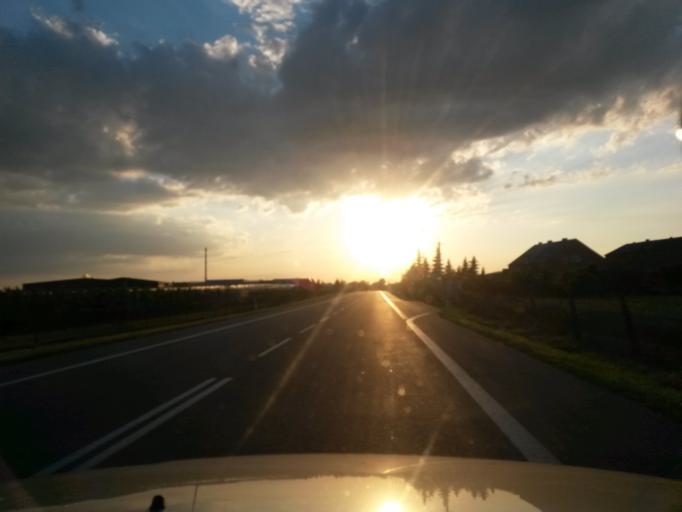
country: PL
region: Lodz Voivodeship
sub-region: Powiat wielunski
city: Czarnozyly
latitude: 51.2559
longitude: 18.4959
